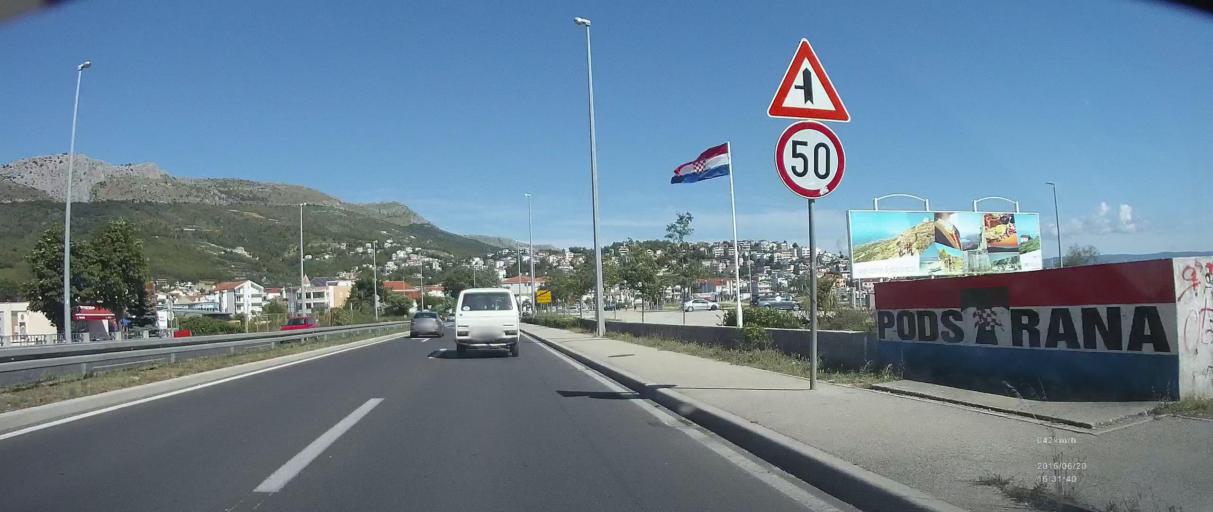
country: HR
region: Splitsko-Dalmatinska
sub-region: Grad Split
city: Stobrec
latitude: 43.5046
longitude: 16.5314
